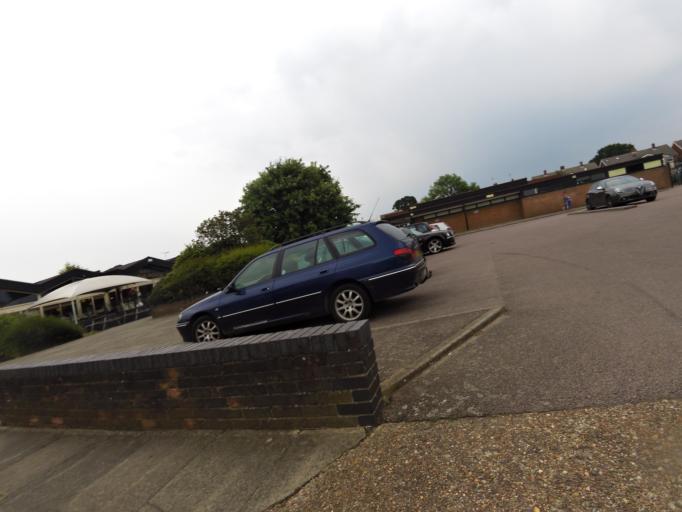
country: GB
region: England
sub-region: Suffolk
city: Ipswich
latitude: 52.0826
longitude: 1.1452
